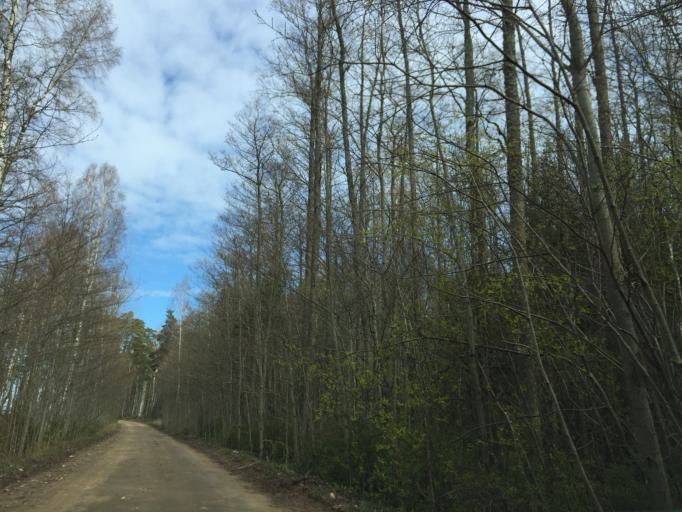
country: LV
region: Salacgrivas
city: Salacgriva
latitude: 57.5832
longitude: 24.3691
